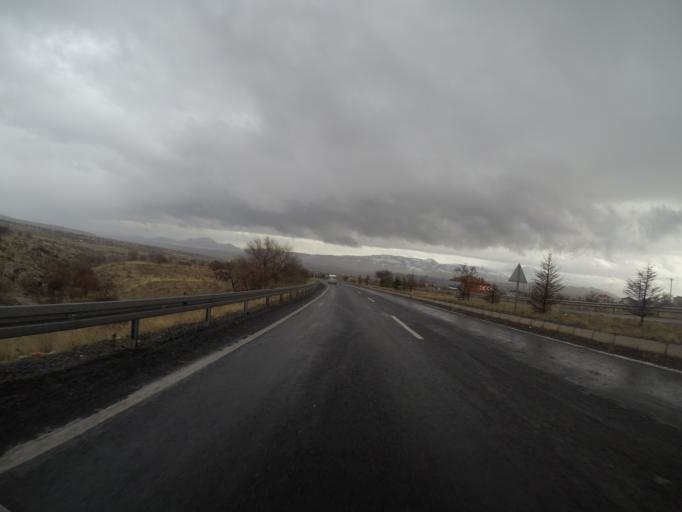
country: TR
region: Kayseri
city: Incesu
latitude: 38.6814
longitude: 35.2022
